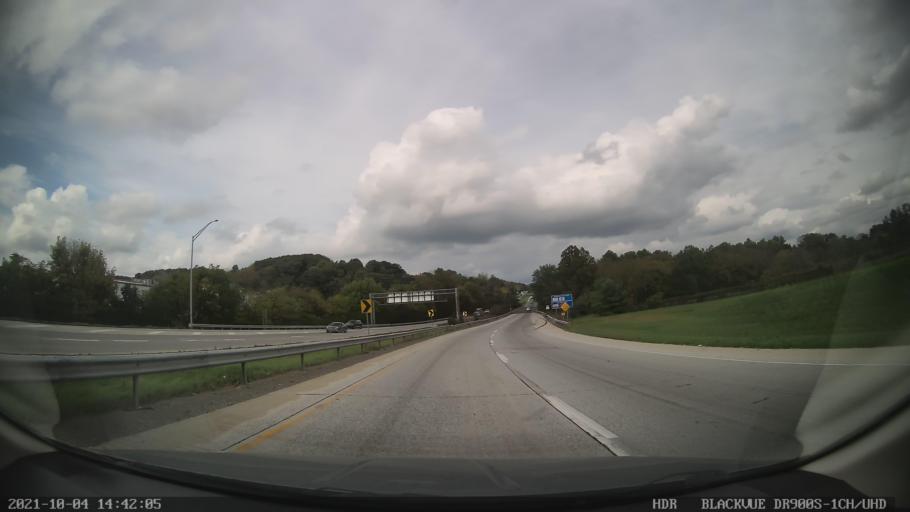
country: US
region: Pennsylvania
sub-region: Berks County
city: Spring Ridge
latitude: 40.3659
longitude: -75.9913
